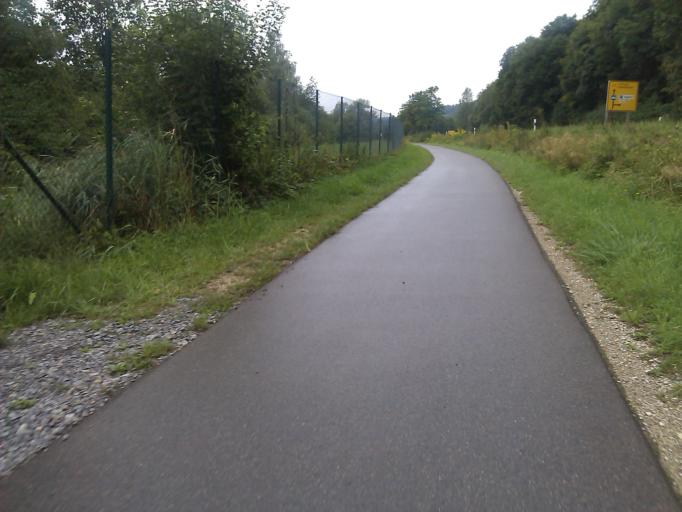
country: DE
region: Baden-Wuerttemberg
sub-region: Tuebingen Region
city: Kirchentellinsfurt
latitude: 48.5476
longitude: 9.1635
